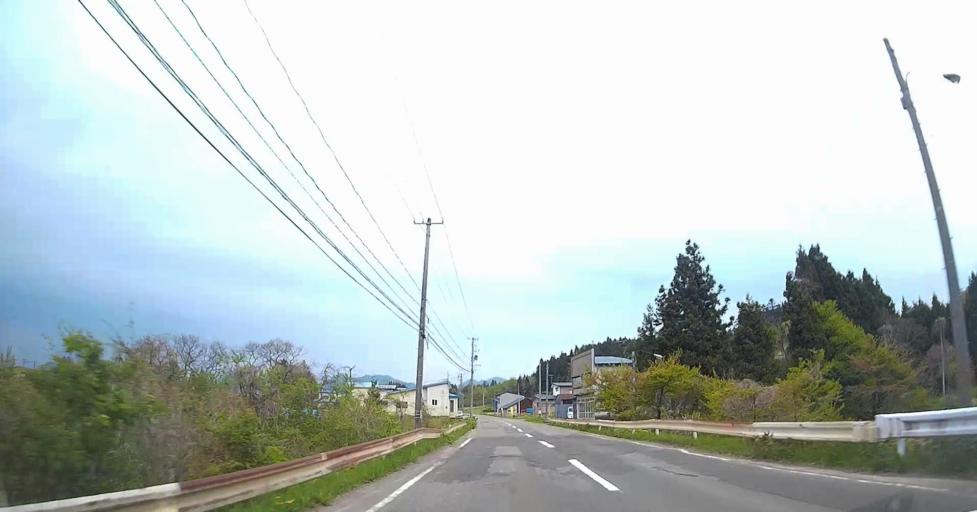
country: JP
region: Aomori
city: Shimokizukuri
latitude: 41.1796
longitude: 140.4638
